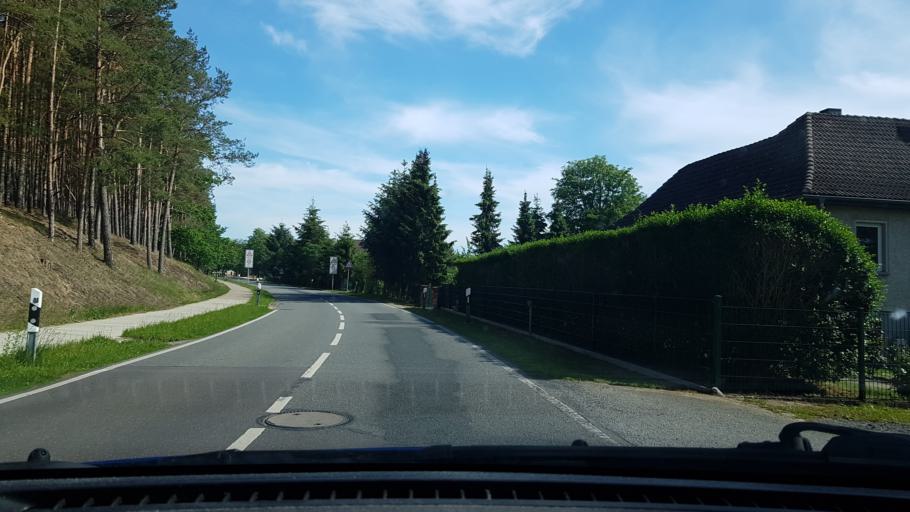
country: DE
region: Lower Saxony
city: Neu Darchau
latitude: 53.2919
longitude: 10.9286
